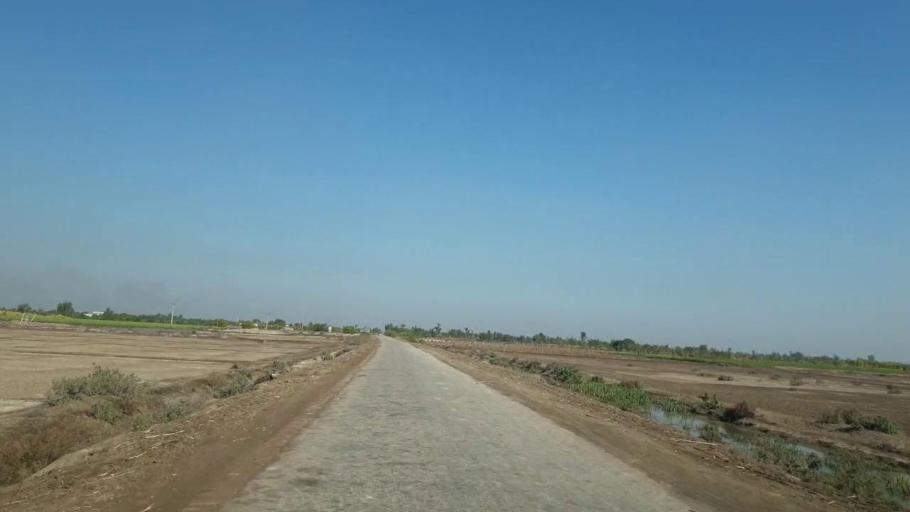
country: PK
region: Sindh
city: Mirpur Khas
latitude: 25.5727
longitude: 69.0463
